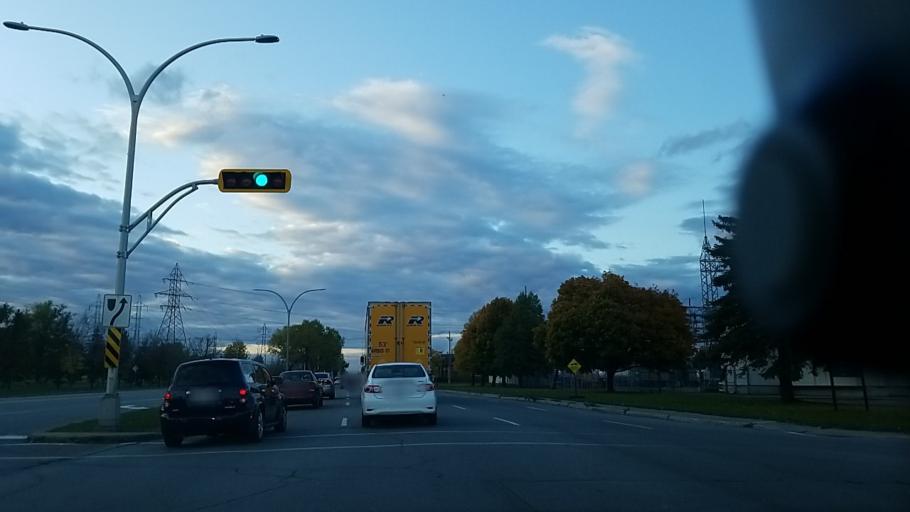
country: CA
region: Quebec
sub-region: Laval
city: Laval
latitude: 45.5747
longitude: -73.7240
